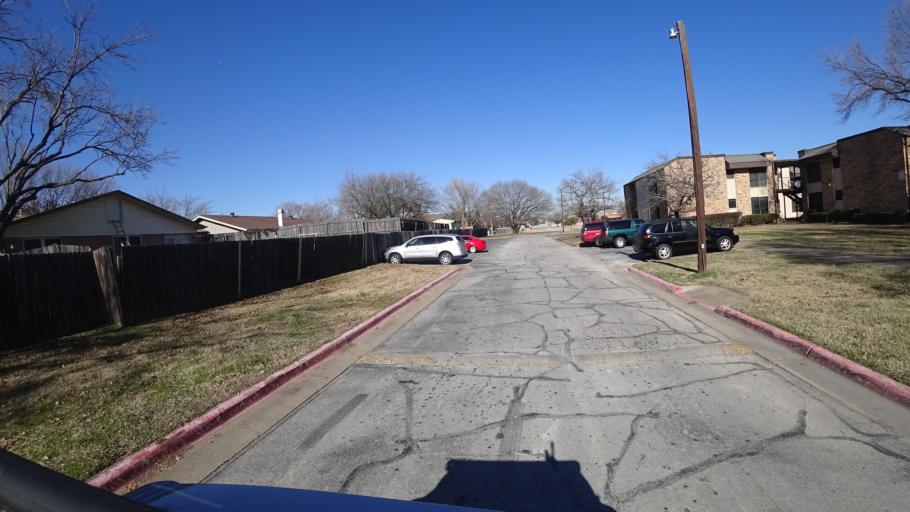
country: US
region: Texas
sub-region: Denton County
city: Lewisville
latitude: 33.0340
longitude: -97.0131
